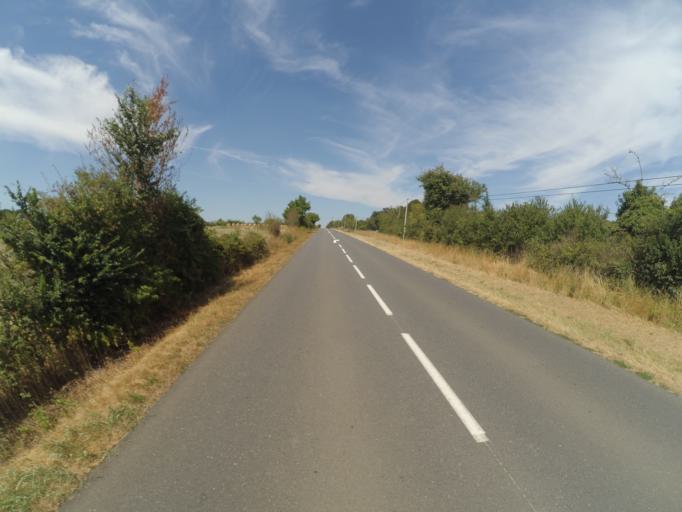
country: FR
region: Poitou-Charentes
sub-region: Departement de la Vienne
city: Usson-du-Poitou
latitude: 46.2372
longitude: 0.5267
